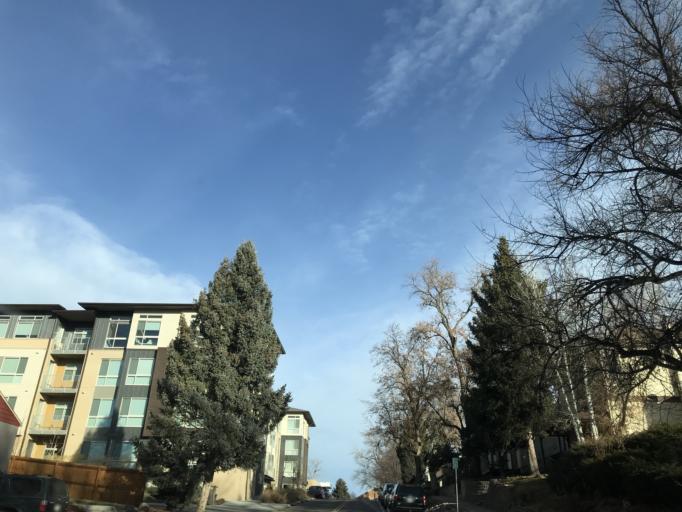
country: US
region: Colorado
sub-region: Arapahoe County
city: Littleton
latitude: 39.6116
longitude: -105.0126
